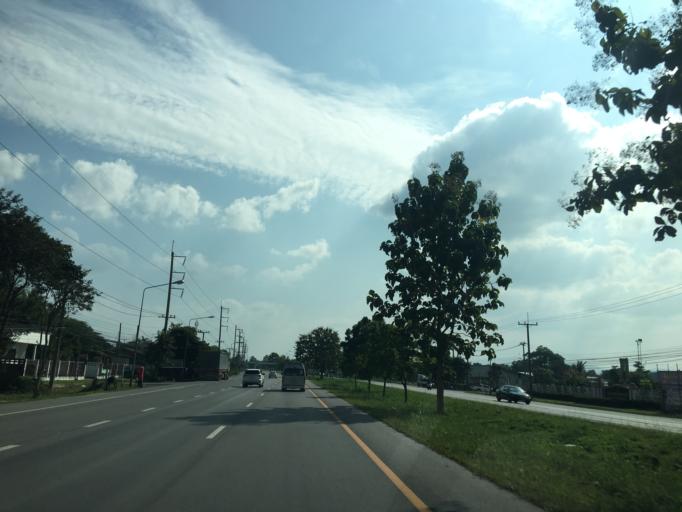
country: TH
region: Chiang Rai
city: Mae Lao
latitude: 19.7245
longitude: 99.7163
